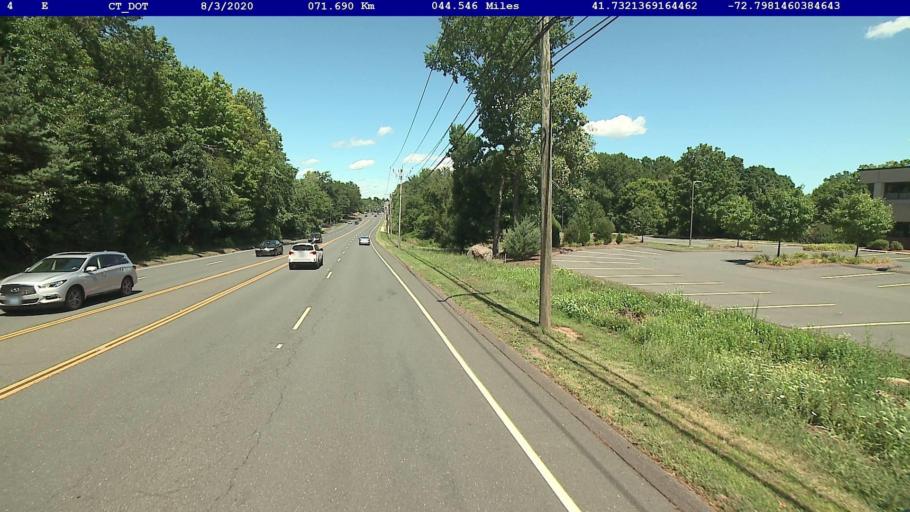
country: US
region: Connecticut
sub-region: Hartford County
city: Farmington
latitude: 41.7321
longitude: -72.7981
